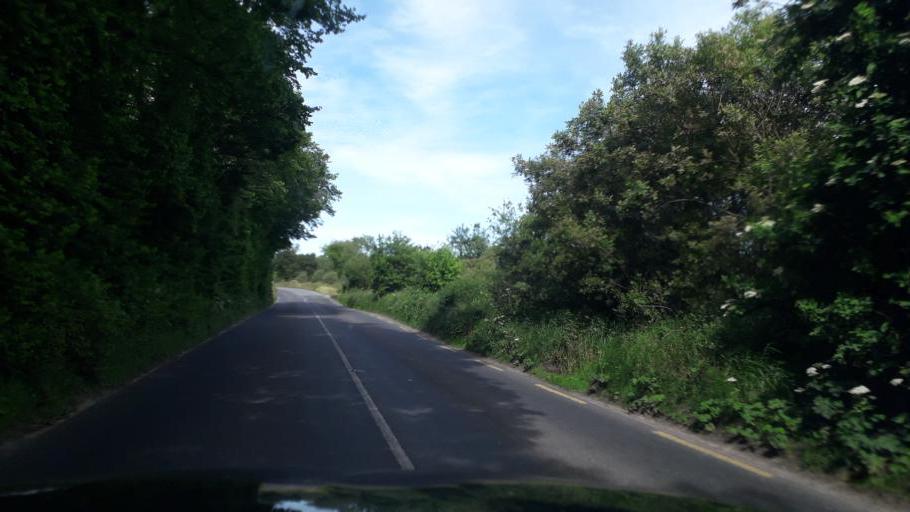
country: IE
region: Leinster
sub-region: Loch Garman
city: Castlebridge
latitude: 52.4036
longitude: -6.4292
